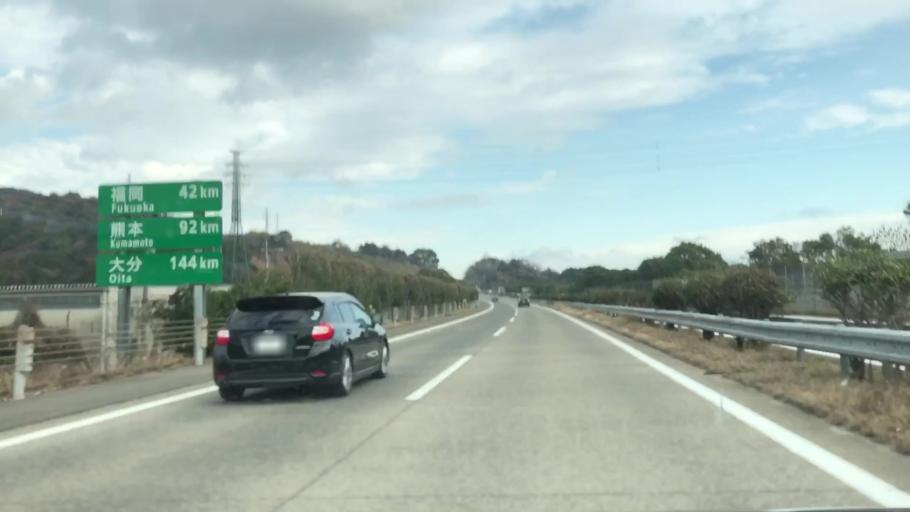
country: JP
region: Saga Prefecture
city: Kanzakimachi-kanzaki
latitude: 33.3546
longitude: 130.4150
